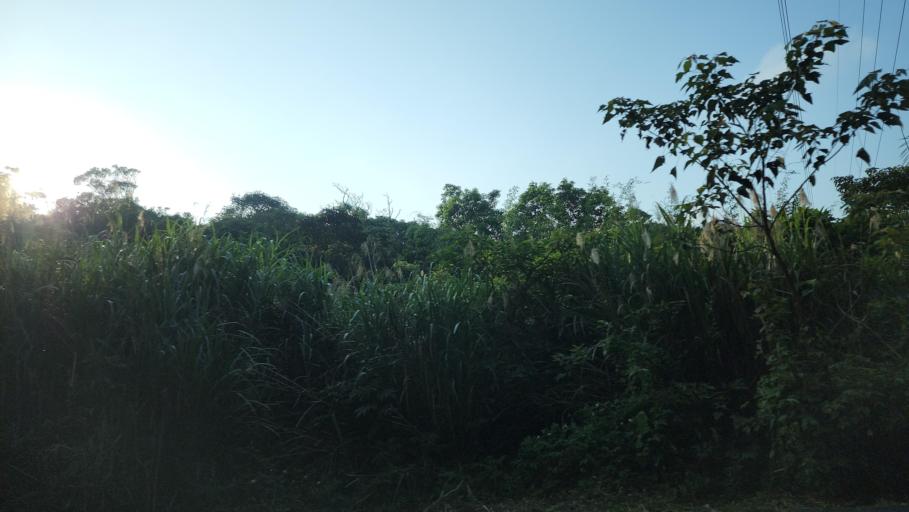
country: TW
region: Taiwan
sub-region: Keelung
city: Keelung
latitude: 25.1757
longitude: 121.6541
